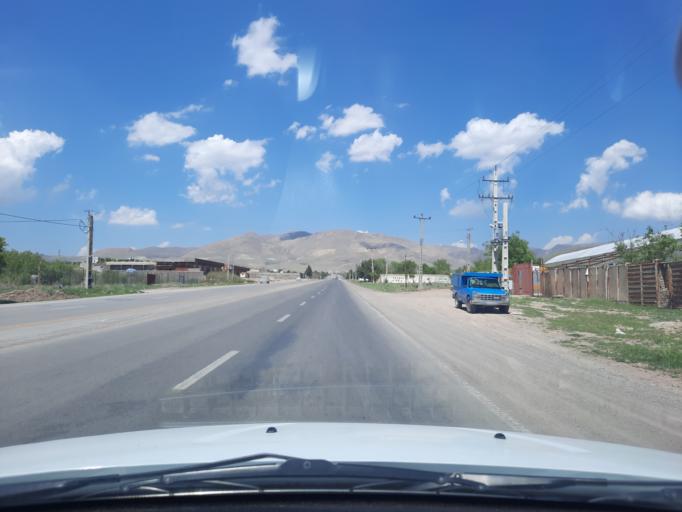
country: IR
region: Qazvin
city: Alvand
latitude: 36.3095
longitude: 50.1450
